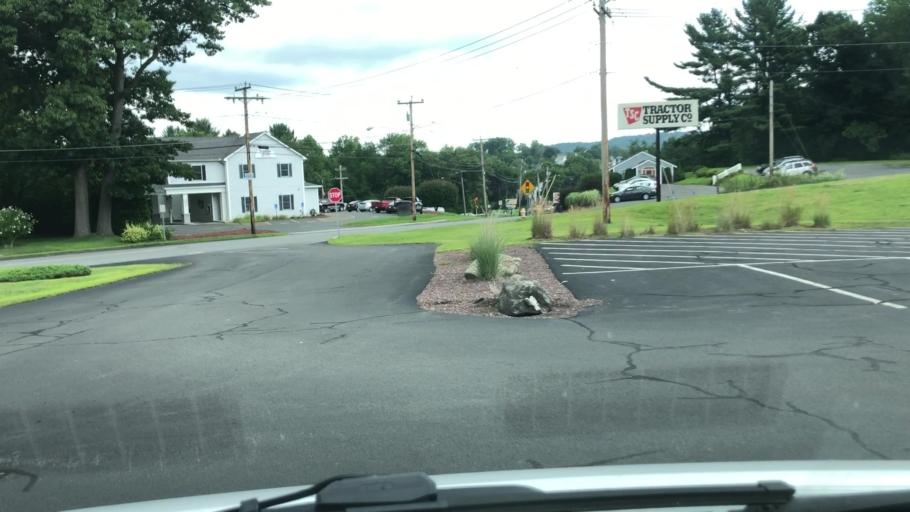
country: US
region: Massachusetts
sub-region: Franklin County
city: Greenfield
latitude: 42.5834
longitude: -72.6176
